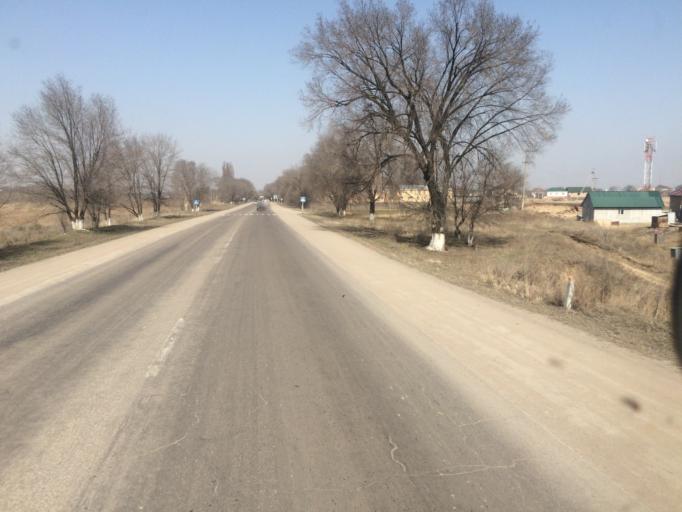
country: KZ
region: Almaty Oblysy
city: Burunday
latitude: 43.2964
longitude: 76.6729
